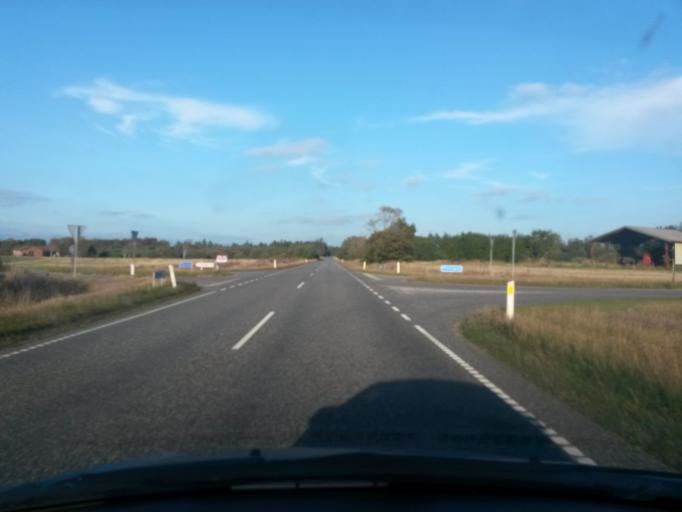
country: DK
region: Central Jutland
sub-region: Herning Kommune
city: Sunds
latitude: 56.3236
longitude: 8.9352
